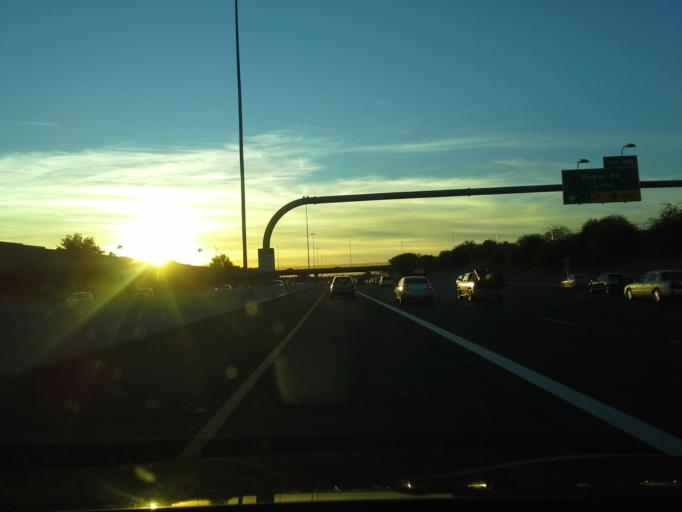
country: US
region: Arizona
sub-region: Maricopa County
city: Gilbert
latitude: 33.3867
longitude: -111.6749
